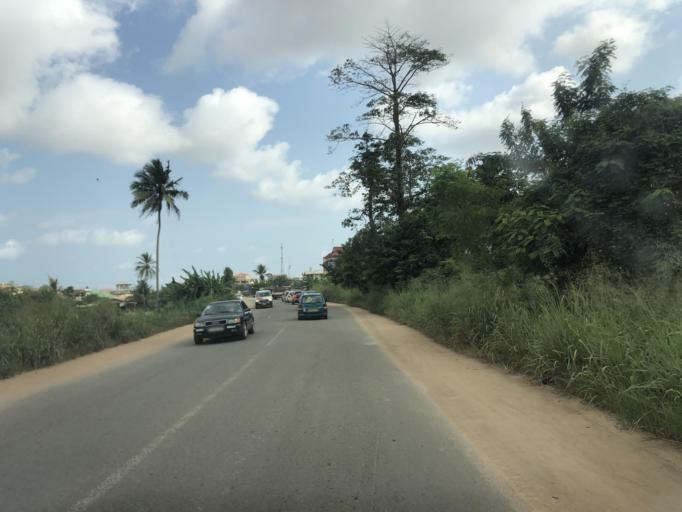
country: GH
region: Central
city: Cape Coast
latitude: 5.1462
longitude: -1.2872
